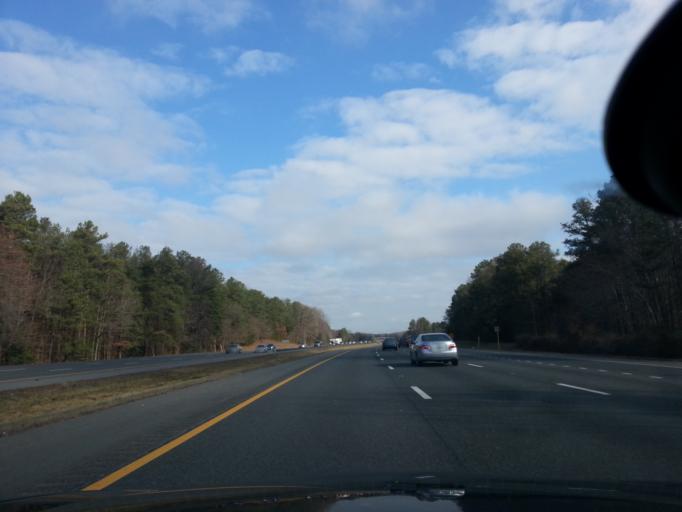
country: US
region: Virginia
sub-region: Caroline County
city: Bowling Green
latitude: 37.9750
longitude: -77.4925
